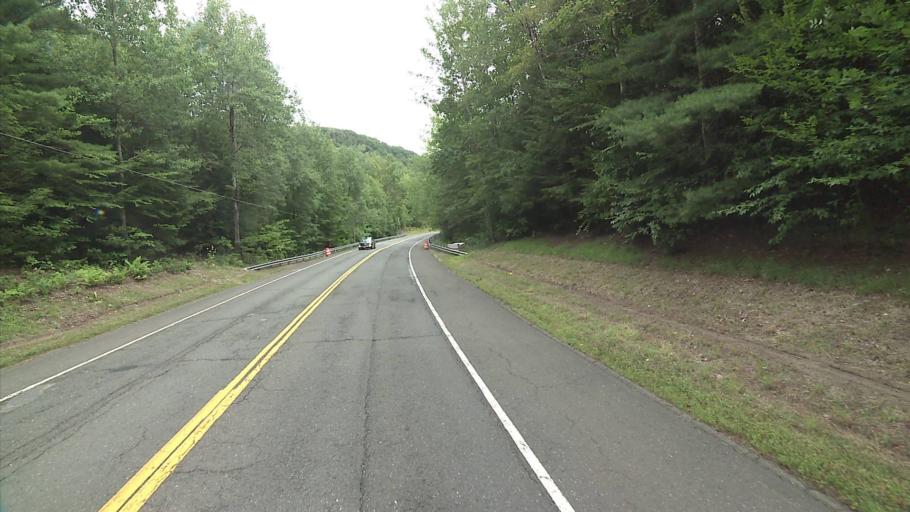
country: US
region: Connecticut
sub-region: Litchfield County
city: Winsted
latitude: 42.0334
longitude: -73.0564
